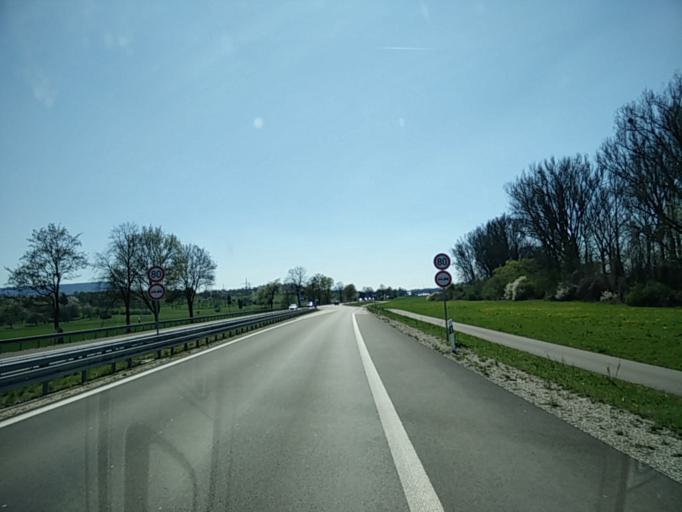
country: DE
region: Baden-Wuerttemberg
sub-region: Tuebingen Region
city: Nehren
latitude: 48.4346
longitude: 9.0543
